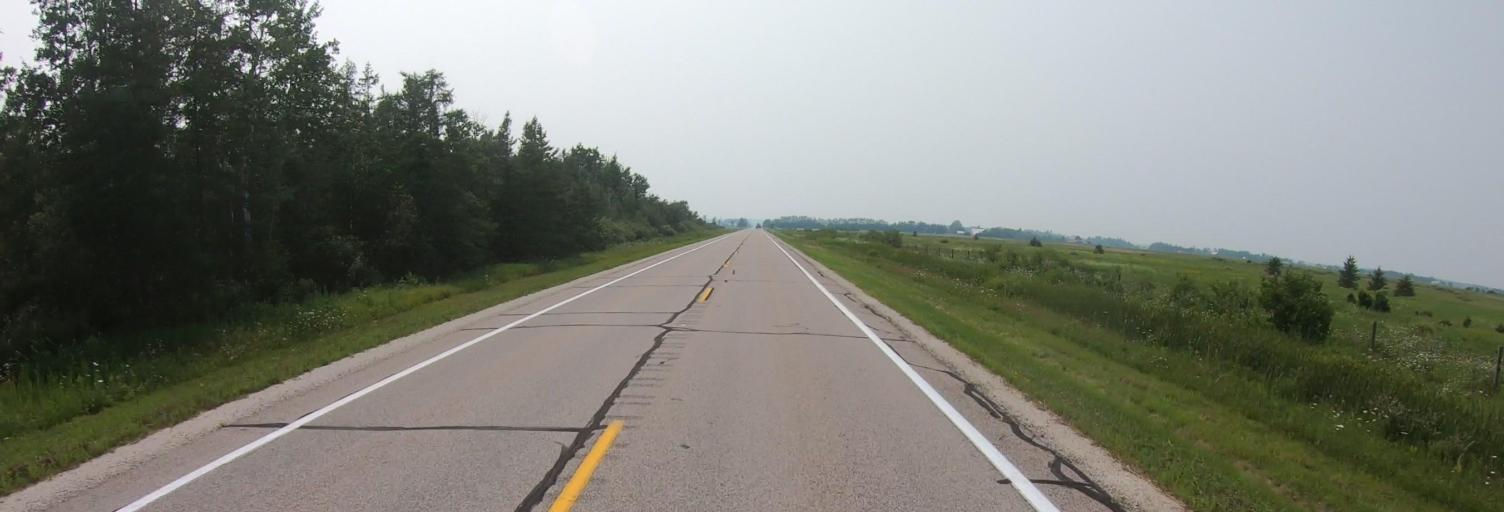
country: US
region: Michigan
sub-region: Chippewa County
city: Sault Ste. Marie
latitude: 46.1292
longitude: -84.3476
